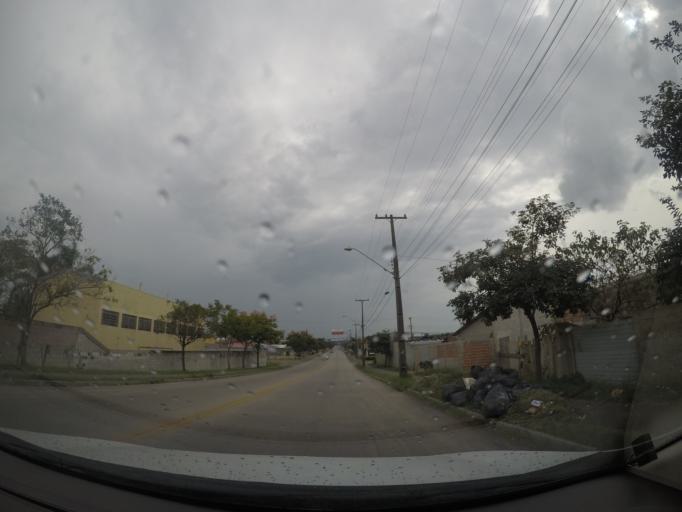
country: BR
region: Parana
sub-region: Sao Jose Dos Pinhais
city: Sao Jose dos Pinhais
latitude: -25.5076
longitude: -49.2153
